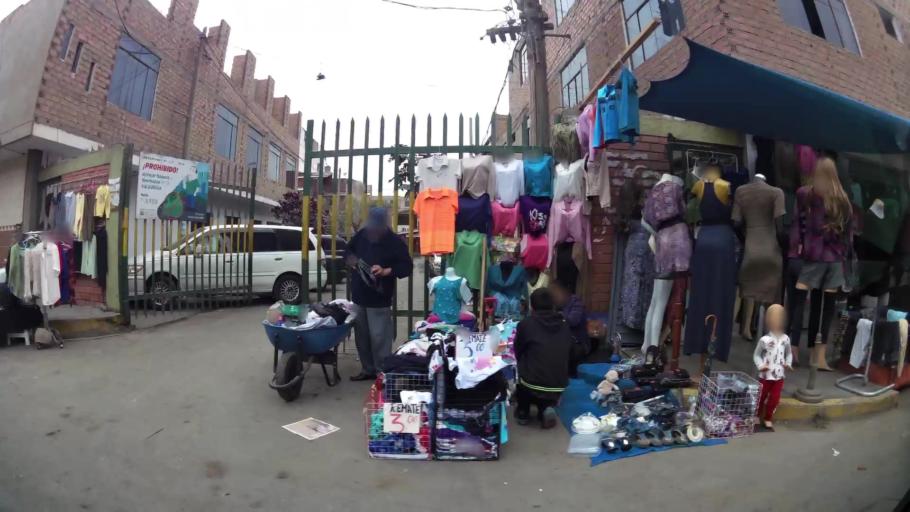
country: PE
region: Lima
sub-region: Lima
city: Independencia
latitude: -11.9609
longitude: -77.0748
